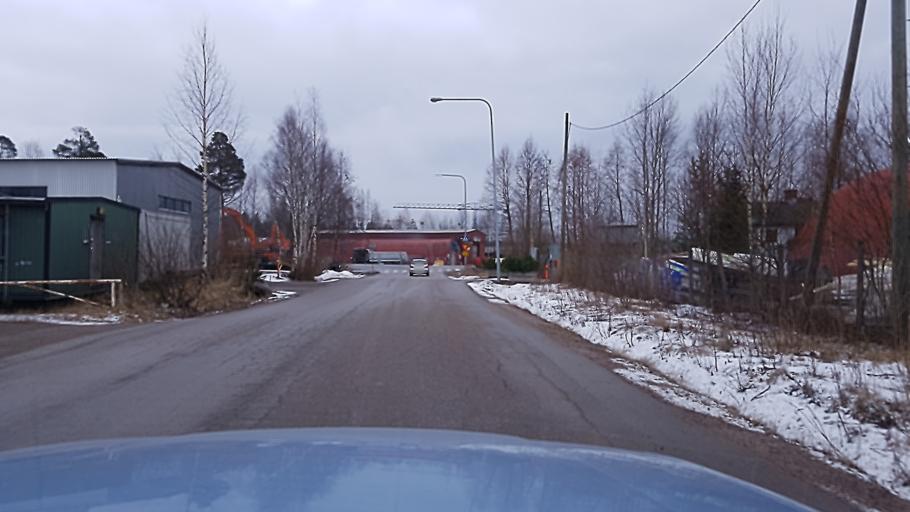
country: FI
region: Uusimaa
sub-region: Helsinki
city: Vantaa
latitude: 60.2591
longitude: 25.0591
